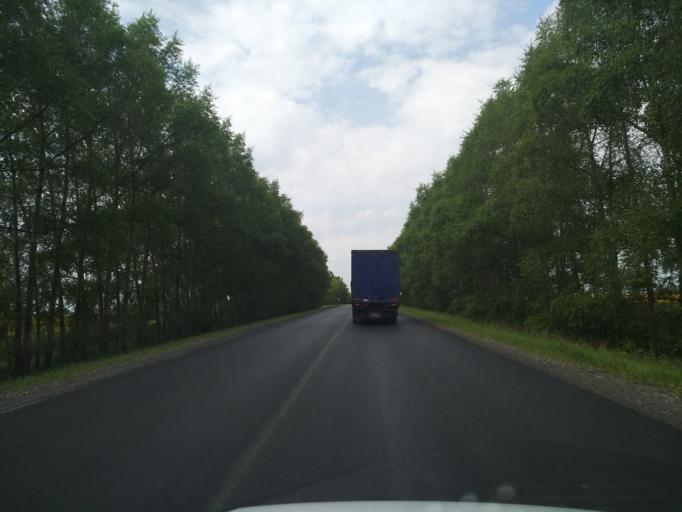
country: RU
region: Voronezj
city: Pereleshino
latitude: 51.7361
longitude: 40.0758
